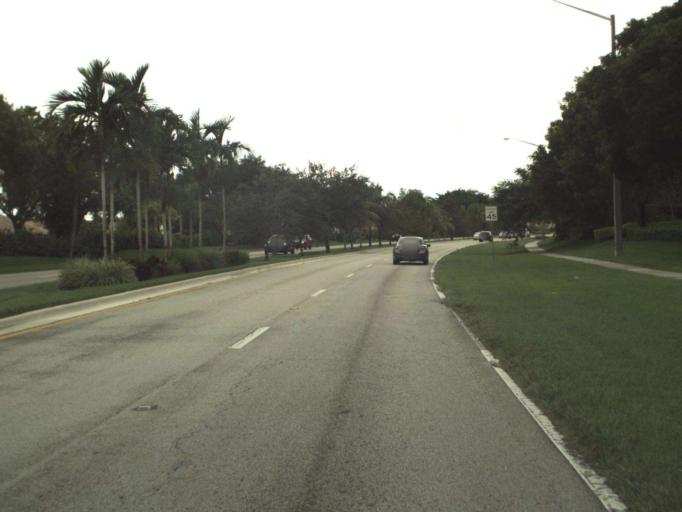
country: US
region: Florida
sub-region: Broward County
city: Coral Springs
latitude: 26.2347
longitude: -80.2856
